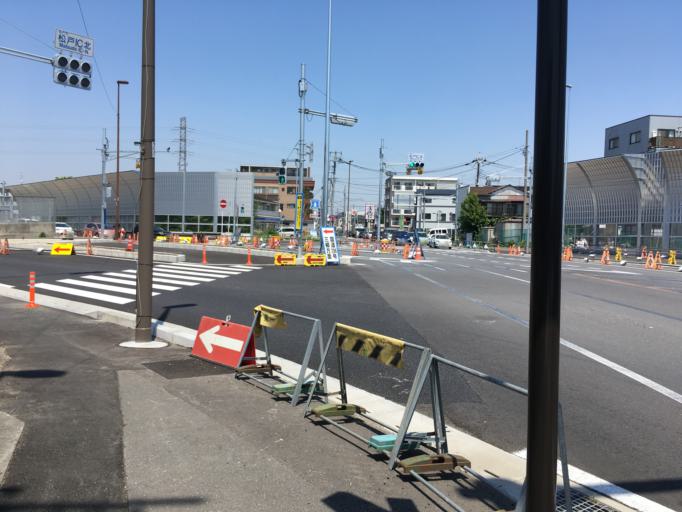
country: JP
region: Chiba
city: Matsudo
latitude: 35.7633
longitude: 139.8992
